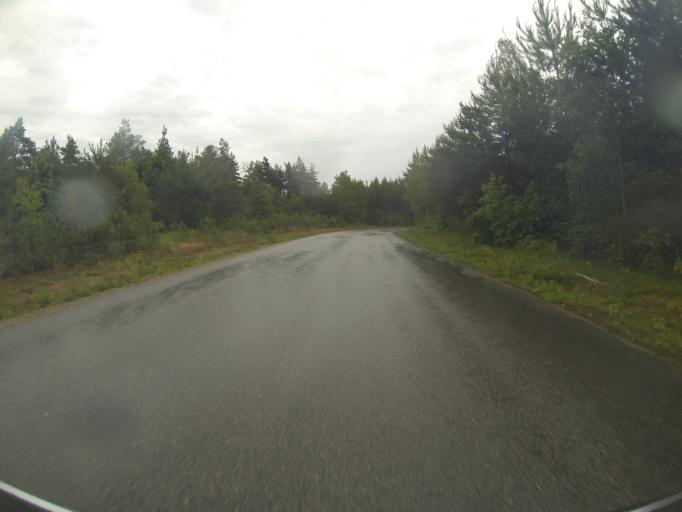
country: SE
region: Blekinge
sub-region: Ronneby Kommun
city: Ronneby
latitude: 56.1701
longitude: 15.3194
